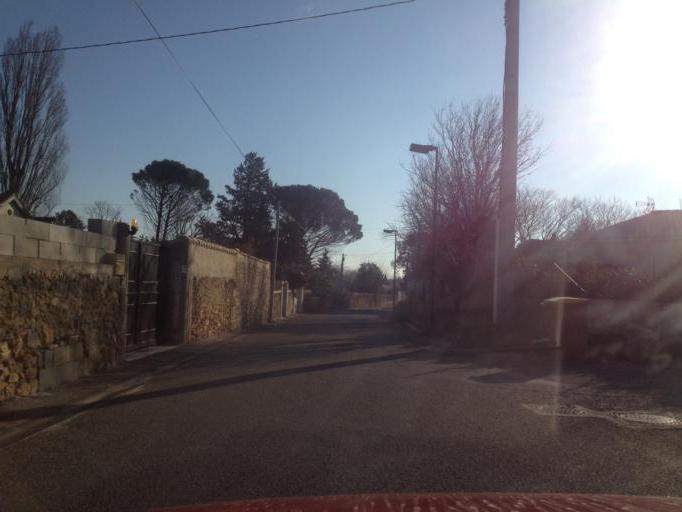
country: FR
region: Provence-Alpes-Cote d'Azur
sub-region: Departement du Vaucluse
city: Orange
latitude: 44.1291
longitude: 4.8265
